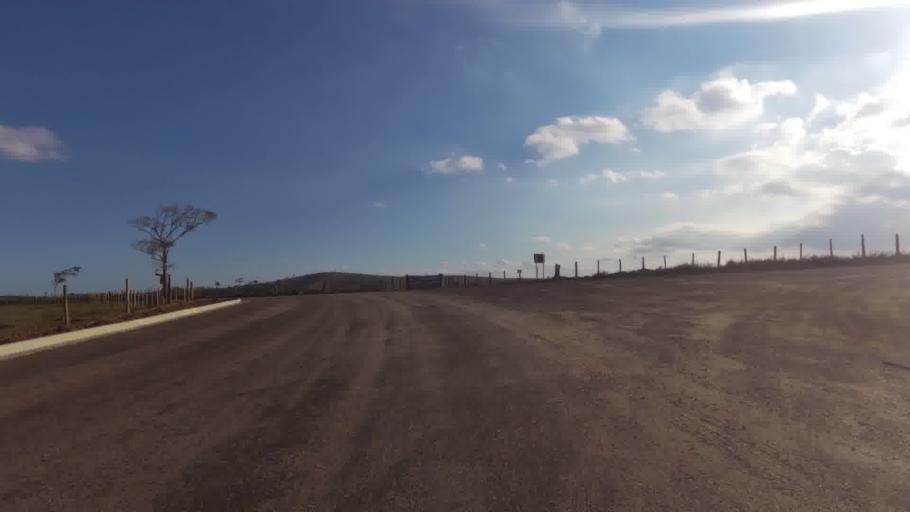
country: BR
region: Espirito Santo
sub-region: Marataizes
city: Marataizes
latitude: -21.1457
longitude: -41.0670
